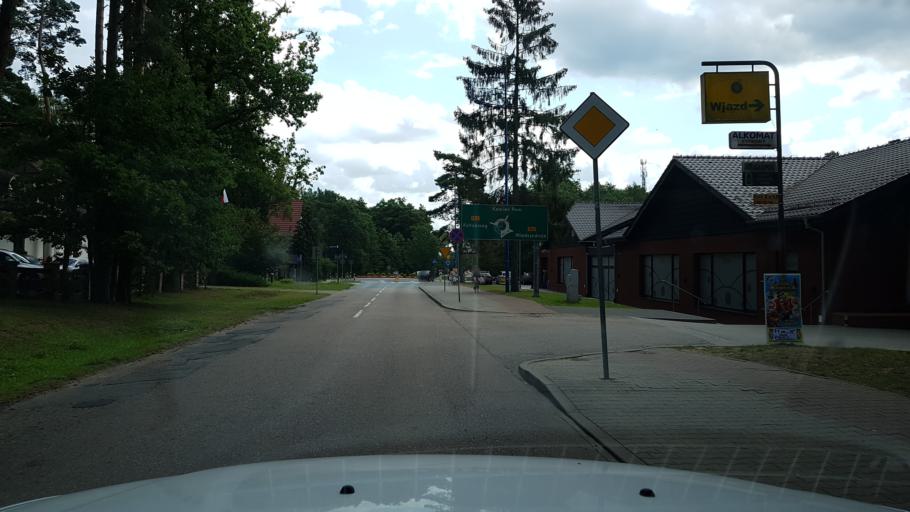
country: PL
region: West Pomeranian Voivodeship
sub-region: Powiat gryficki
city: Pobierowo
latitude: 54.0561
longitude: 14.9412
